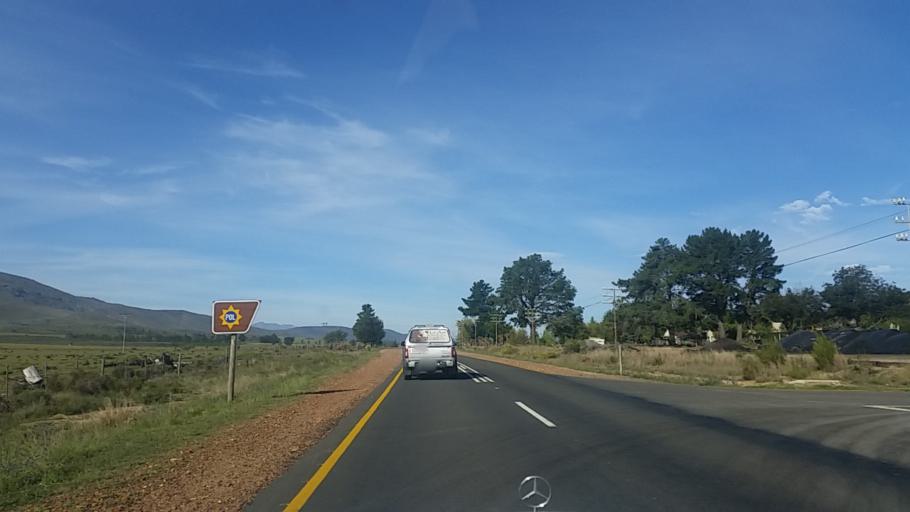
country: ZA
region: Western Cape
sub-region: Eden District Municipality
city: George
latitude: -33.8336
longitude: 22.4516
